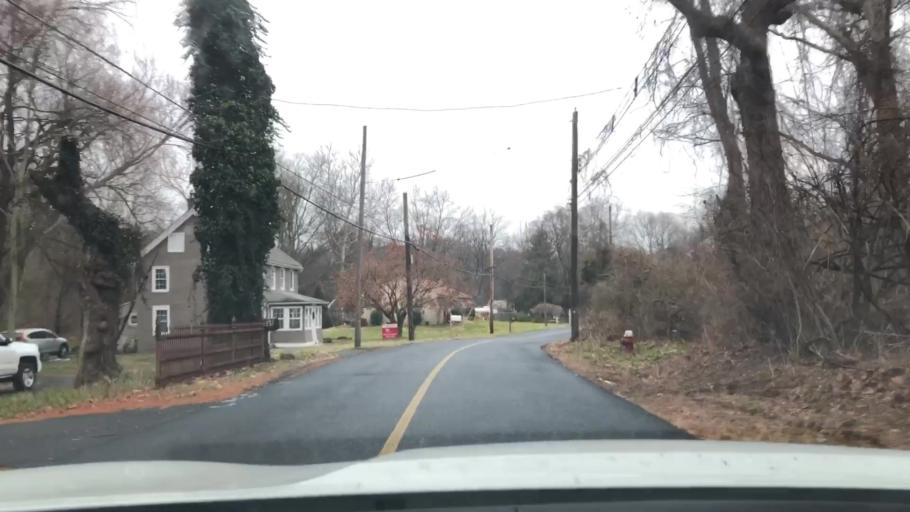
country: US
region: Pennsylvania
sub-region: Chester County
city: Spring City
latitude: 40.1974
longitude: -75.5796
